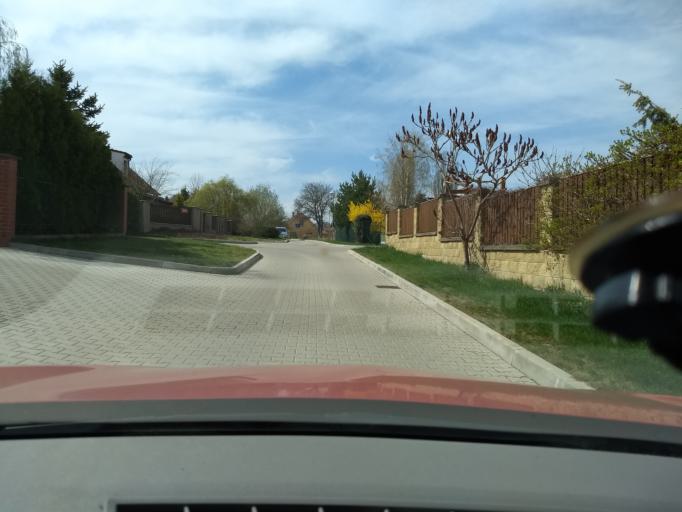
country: CZ
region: Central Bohemia
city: Unhost'
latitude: 50.0506
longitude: 14.1726
